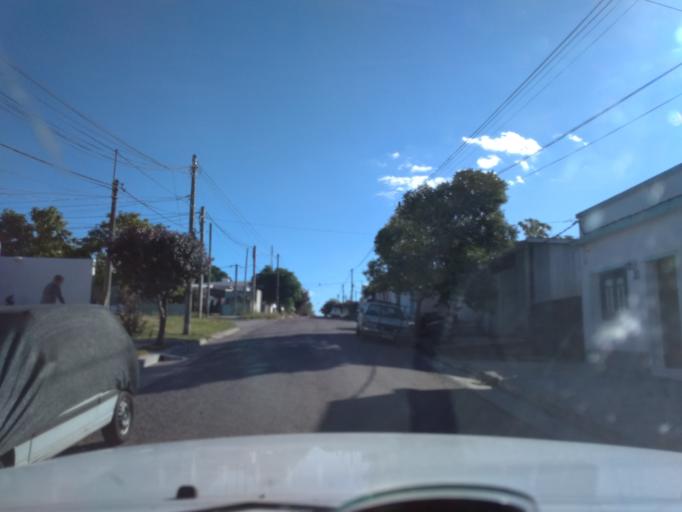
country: UY
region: Florida
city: Florida
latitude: -34.0935
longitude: -56.2085
